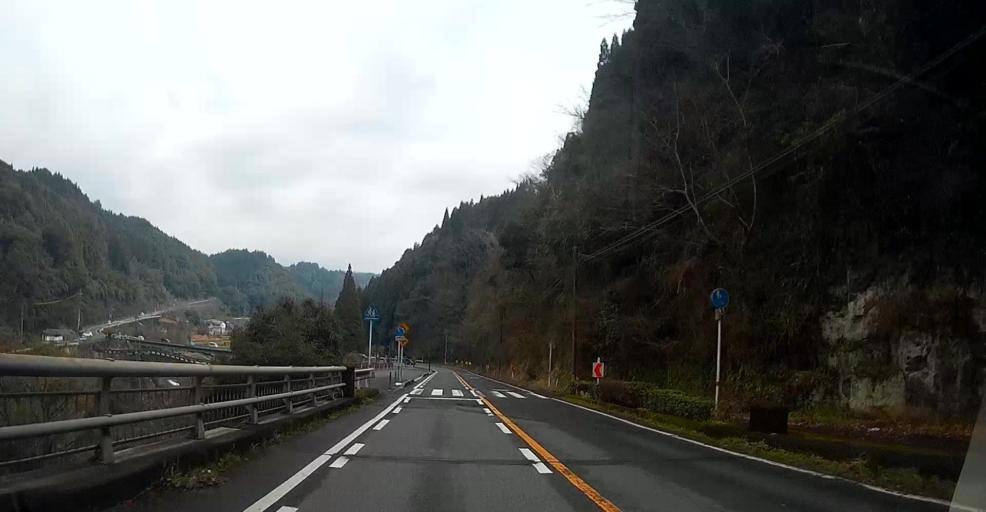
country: JP
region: Kumamoto
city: Matsubase
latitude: 32.6280
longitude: 130.8876
